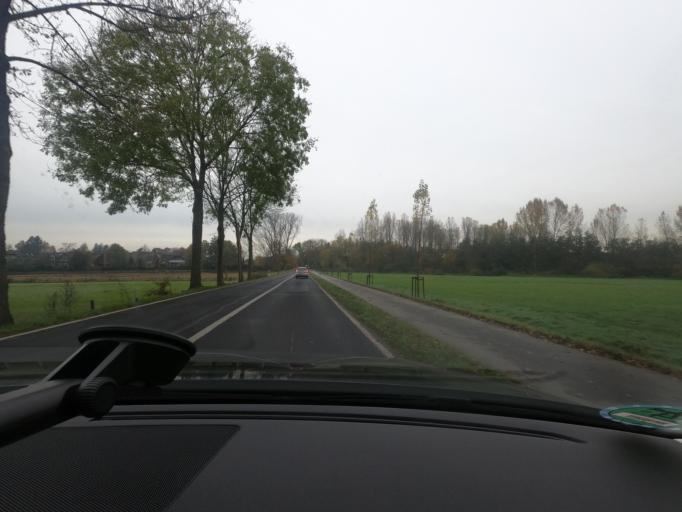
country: DE
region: North Rhine-Westphalia
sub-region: Regierungsbezirk Dusseldorf
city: Kevelaer
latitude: 51.5938
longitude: 6.2916
